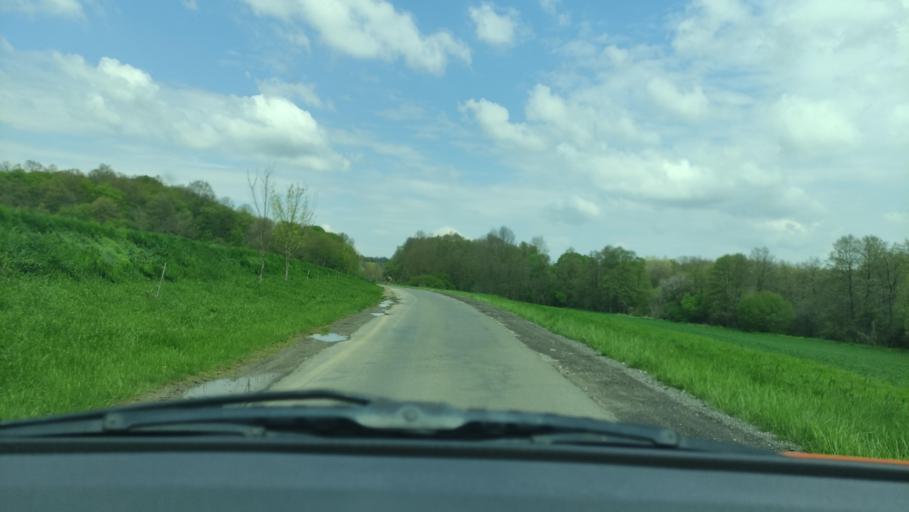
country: HU
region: Baranya
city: Sasd
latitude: 46.2820
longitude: 18.1051
